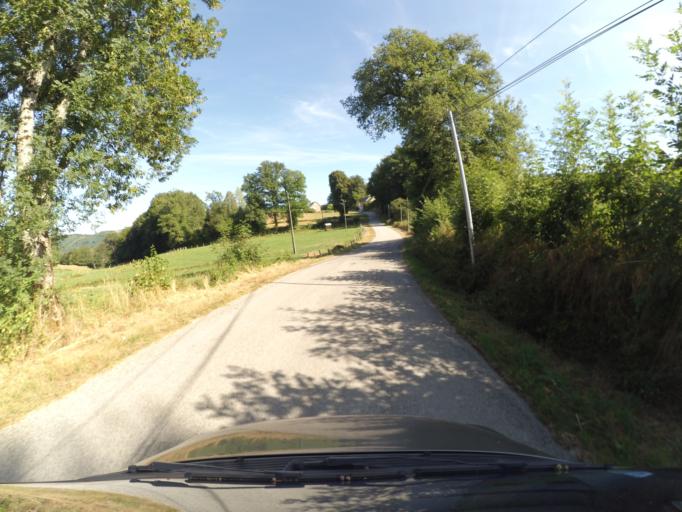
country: FR
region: Limousin
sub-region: Departement de la Correze
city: Bugeat
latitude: 45.6909
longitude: 1.8869
